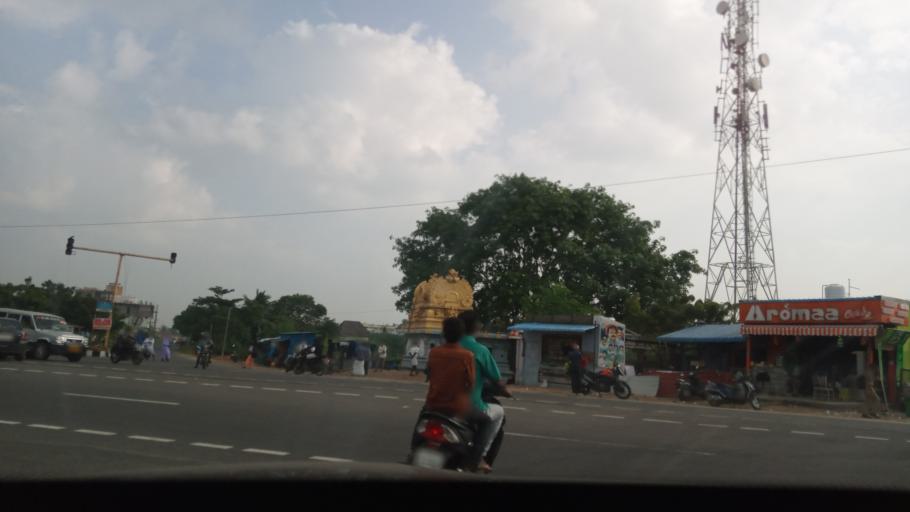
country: IN
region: Tamil Nadu
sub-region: Kancheepuram
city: Injambakkam
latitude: 12.7845
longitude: 80.2450
